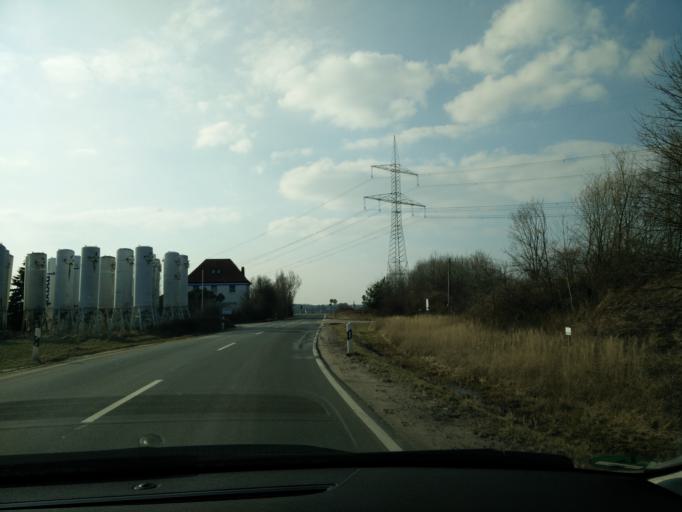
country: DE
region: Saxony
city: Konigsfeld
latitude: 51.0992
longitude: 12.7490
